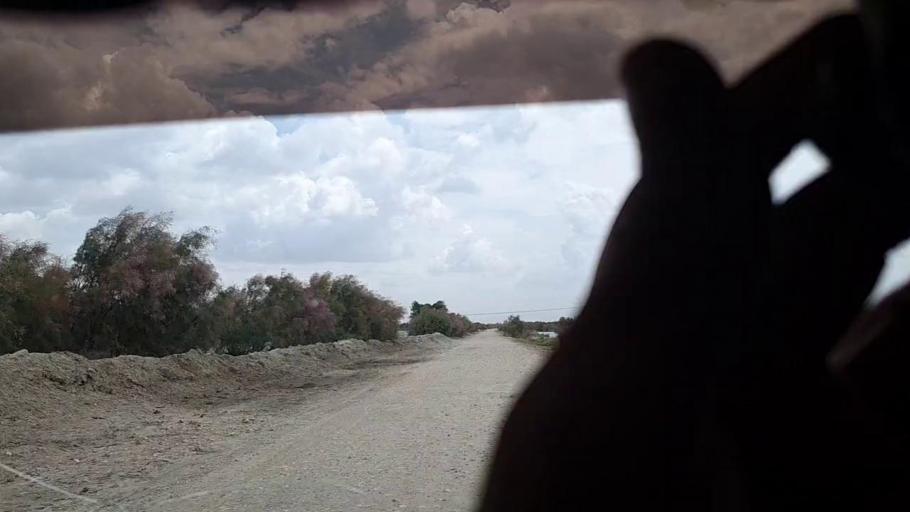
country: PK
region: Sindh
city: Ghauspur
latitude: 28.0706
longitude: 68.9370
